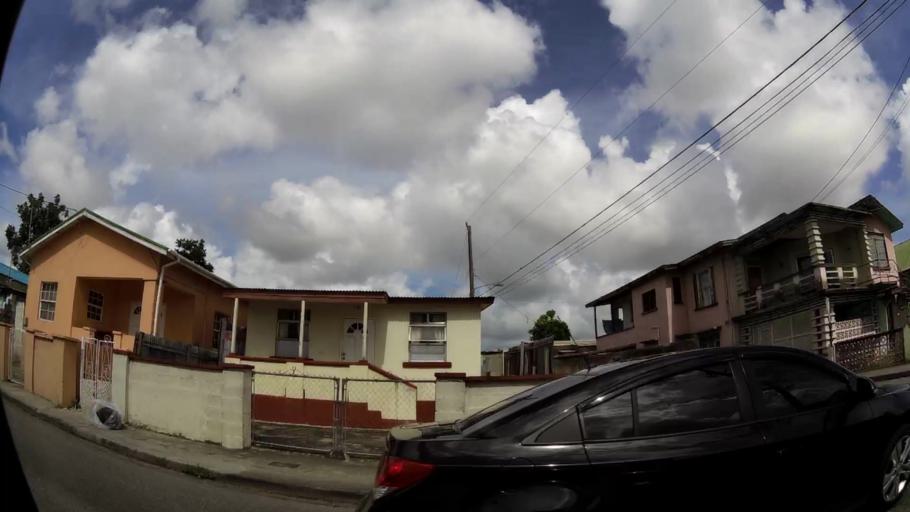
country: BB
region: Saint Michael
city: Bridgetown
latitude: 13.1120
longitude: -59.6127
